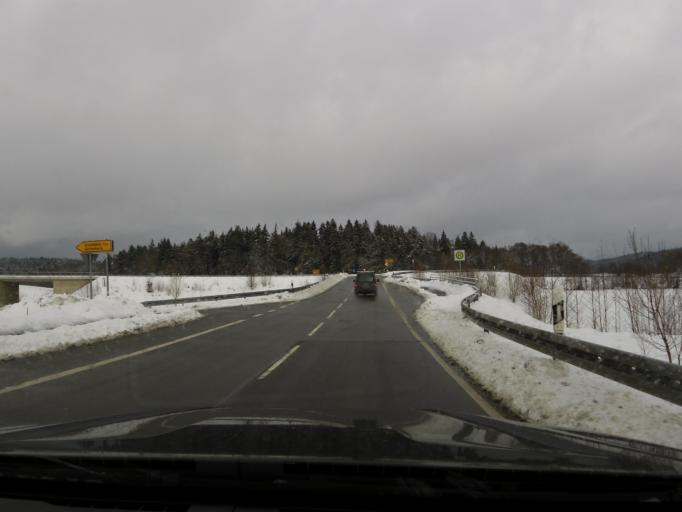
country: DE
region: Bavaria
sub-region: Lower Bavaria
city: Auerbach
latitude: 48.7902
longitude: 13.0796
